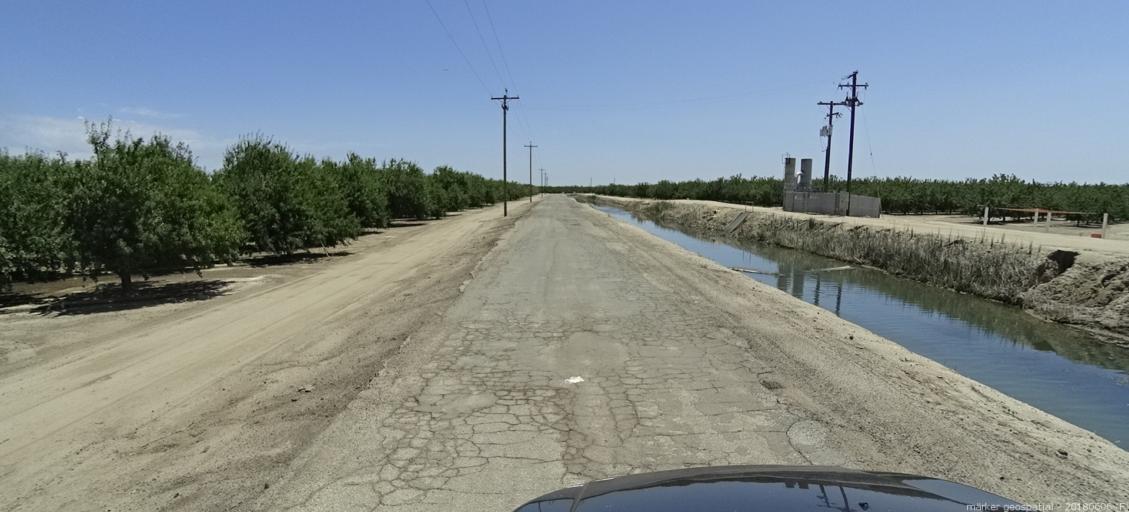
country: US
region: California
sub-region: Fresno County
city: Mendota
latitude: 36.7888
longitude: -120.3141
